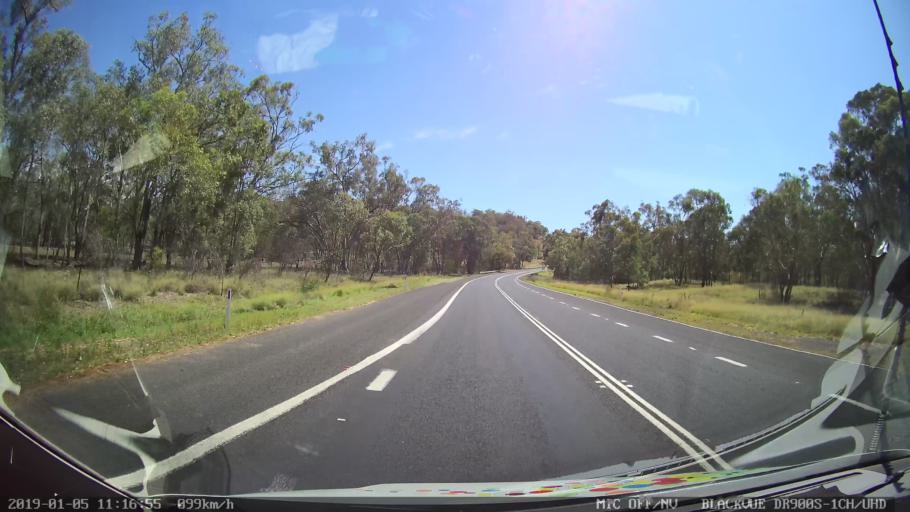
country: AU
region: New South Wales
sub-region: Warrumbungle Shire
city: Coonabarabran
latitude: -31.3323
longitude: 149.3018
